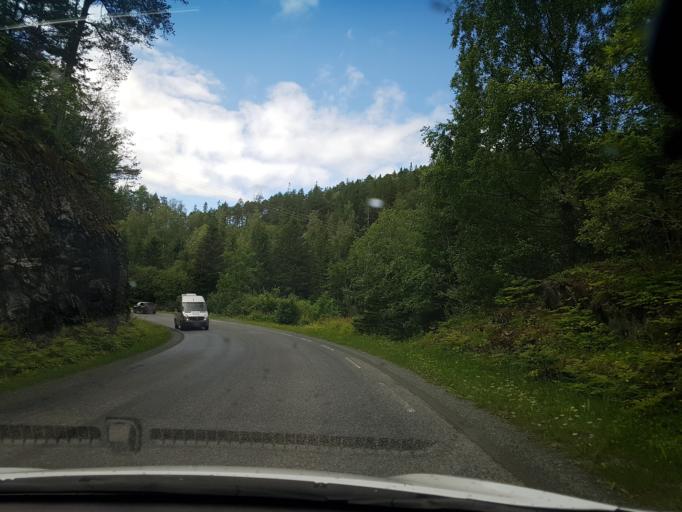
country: NO
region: Nord-Trondelag
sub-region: Stjordal
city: Stjordalshalsen
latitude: 63.6080
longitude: 10.9528
